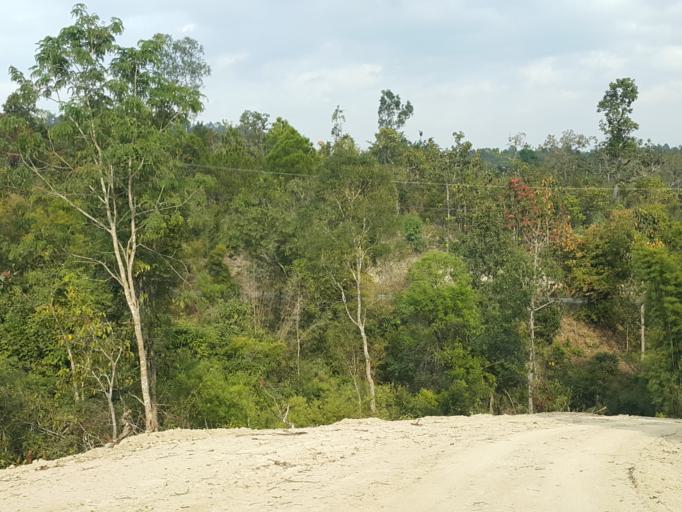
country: TH
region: Chiang Mai
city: Om Koi
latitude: 17.7984
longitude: 98.3404
